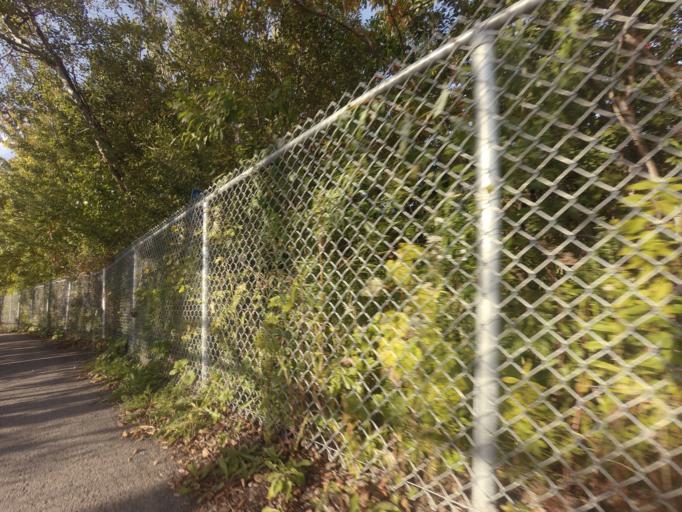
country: CA
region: Quebec
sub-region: Laurentides
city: Saint-Jerome
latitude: 45.7544
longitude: -73.9753
